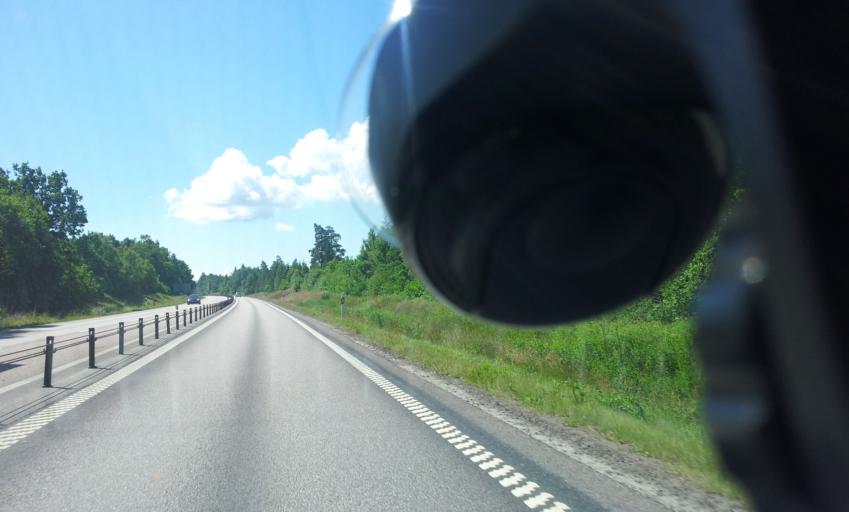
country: SE
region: Kalmar
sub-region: Oskarshamns Kommun
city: Paskallavik
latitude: 57.1940
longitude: 16.4383
